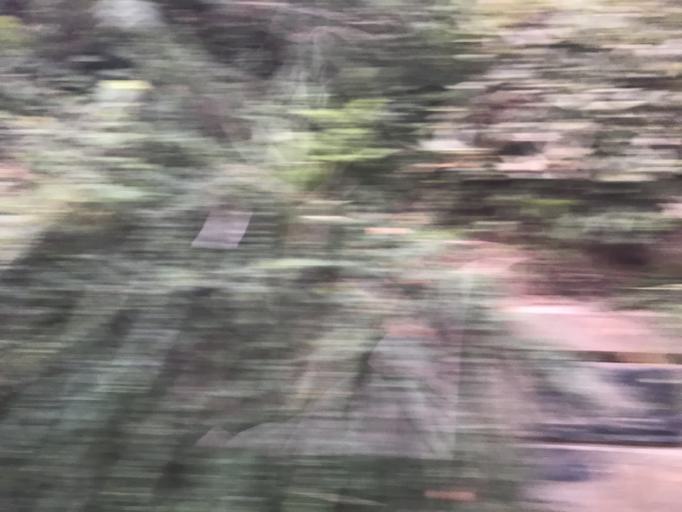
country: KR
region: Seoul
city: Seoul
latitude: 37.5661
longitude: 126.9457
